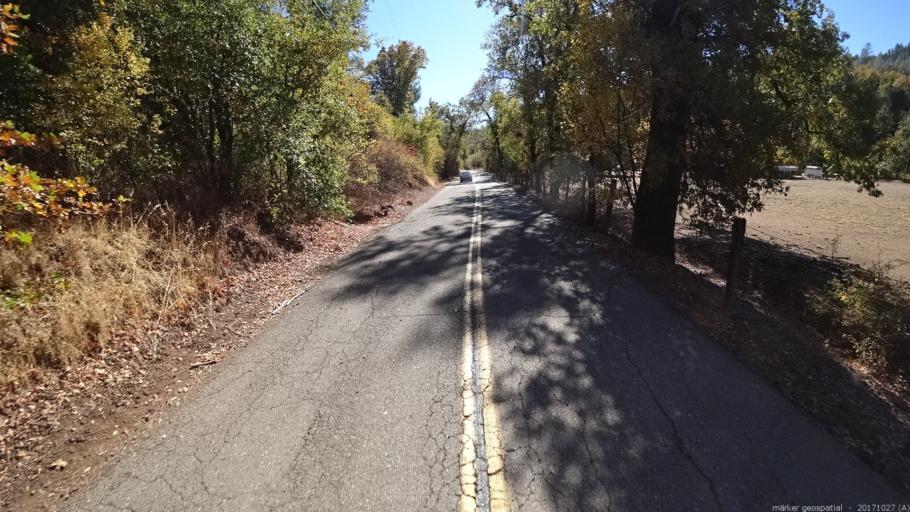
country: US
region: California
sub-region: Shasta County
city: Bella Vista
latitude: 40.7481
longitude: -122.0201
